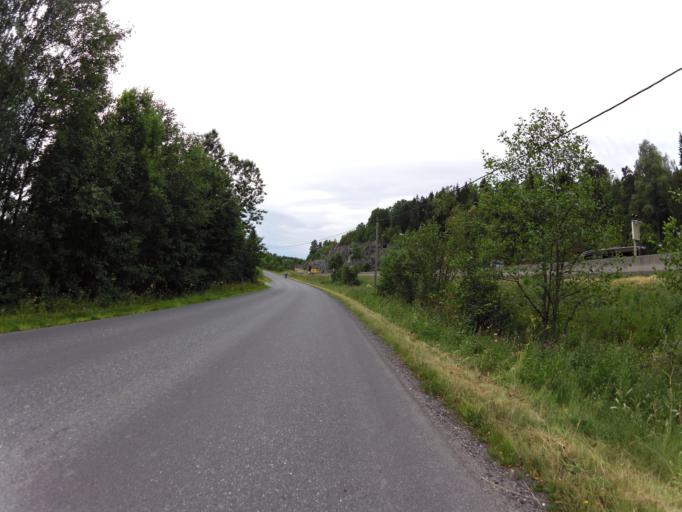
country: NO
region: Akershus
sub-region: As
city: As
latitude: 59.6929
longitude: 10.7339
